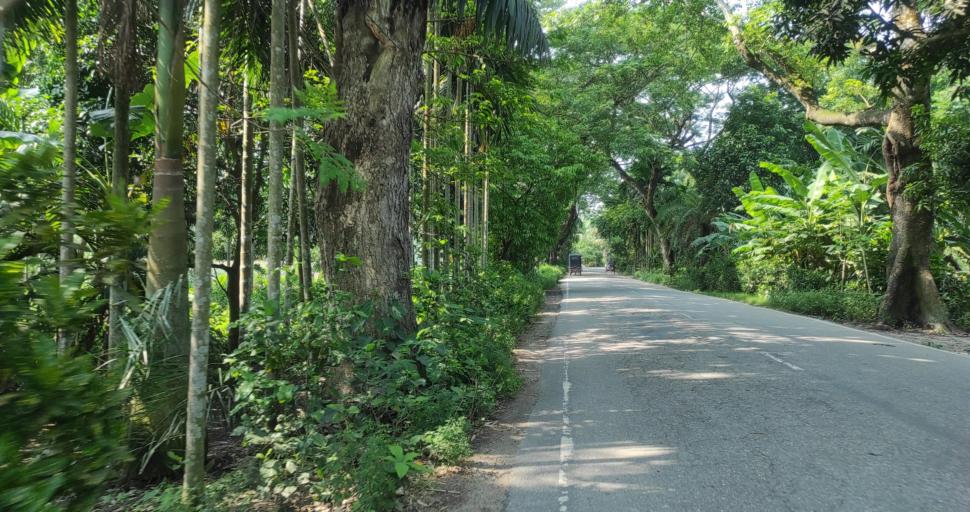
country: BD
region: Rajshahi
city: Ishurdi
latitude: 24.2851
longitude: 89.0653
